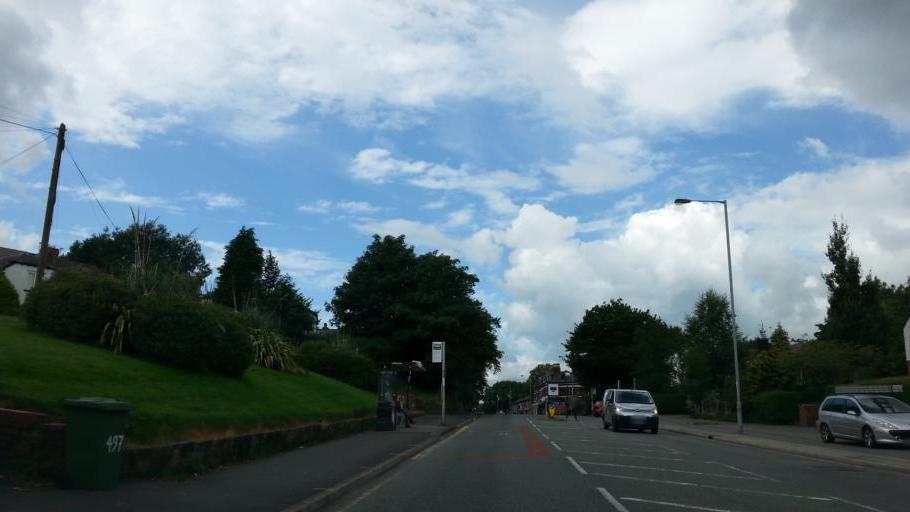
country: GB
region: England
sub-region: Borough of Bury
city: Prestwich
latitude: 53.5381
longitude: -2.2780
